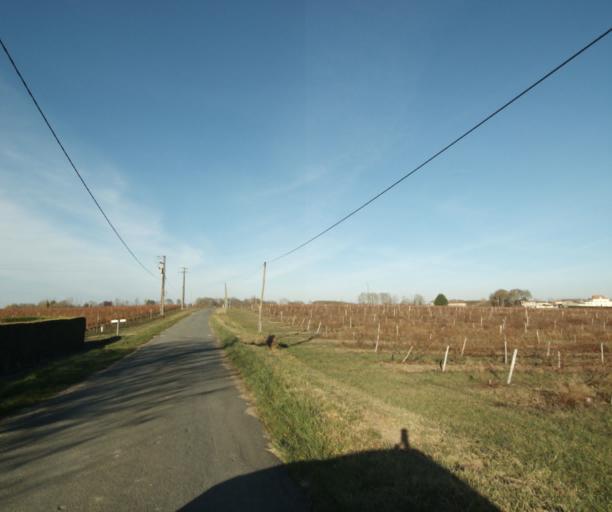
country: FR
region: Poitou-Charentes
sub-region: Departement de la Charente-Maritime
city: Burie
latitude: 45.7847
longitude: -0.4173
